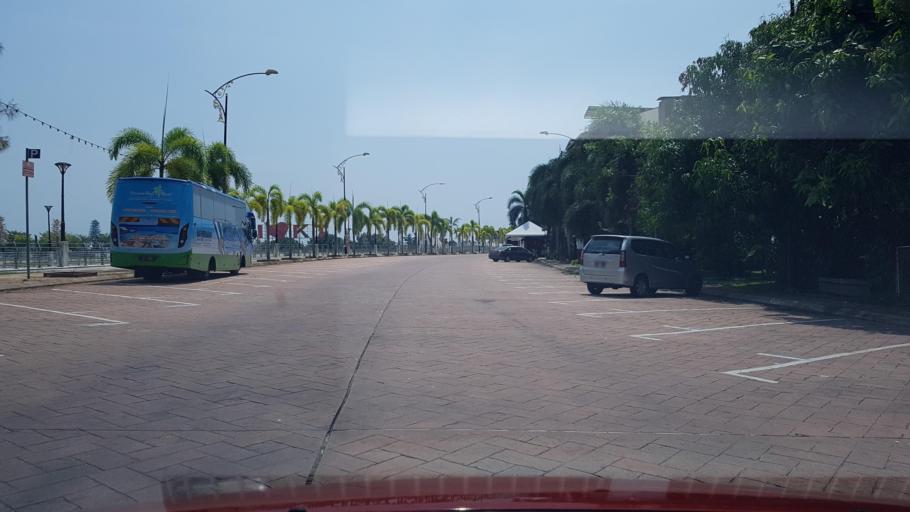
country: MY
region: Terengganu
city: Kuala Terengganu
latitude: 5.3337
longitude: 103.1324
